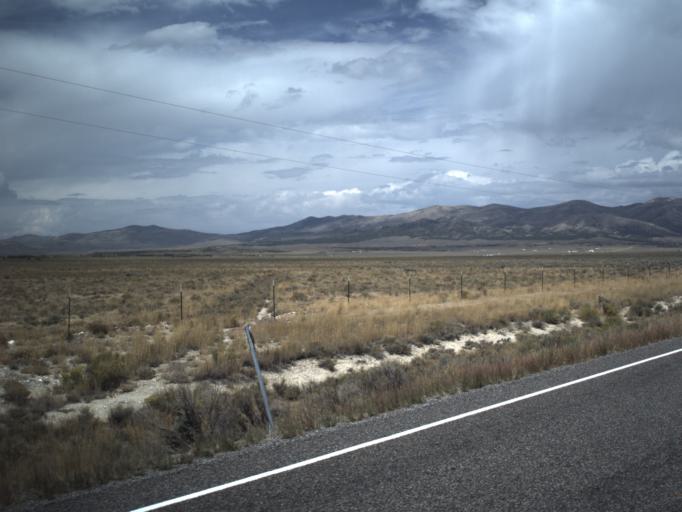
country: US
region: Idaho
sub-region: Cassia County
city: Burley
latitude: 41.7470
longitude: -113.5171
